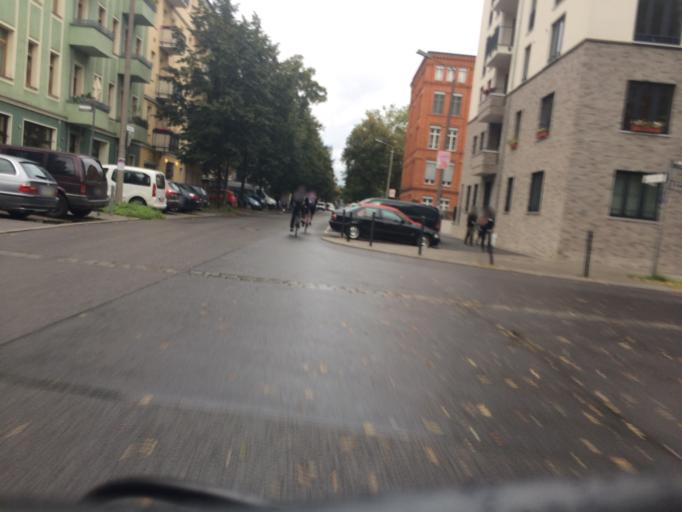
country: DE
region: Berlin
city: Treptow Bezirk
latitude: 52.4867
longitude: 13.4510
